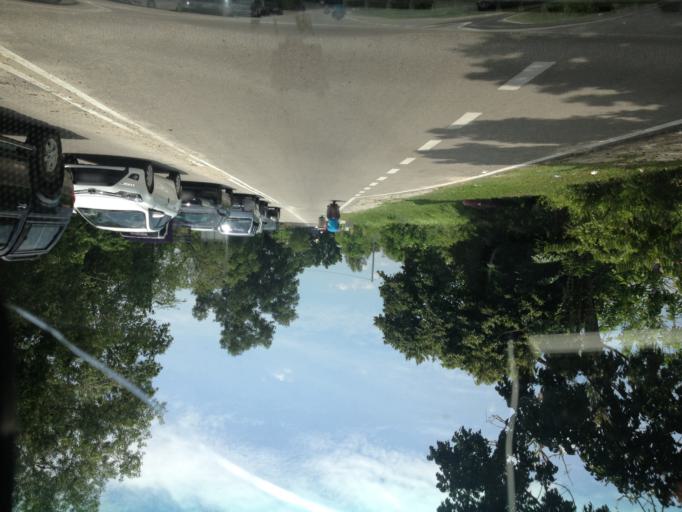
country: MY
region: Kedah
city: Sungai Petani
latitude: 5.6327
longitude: 100.5182
